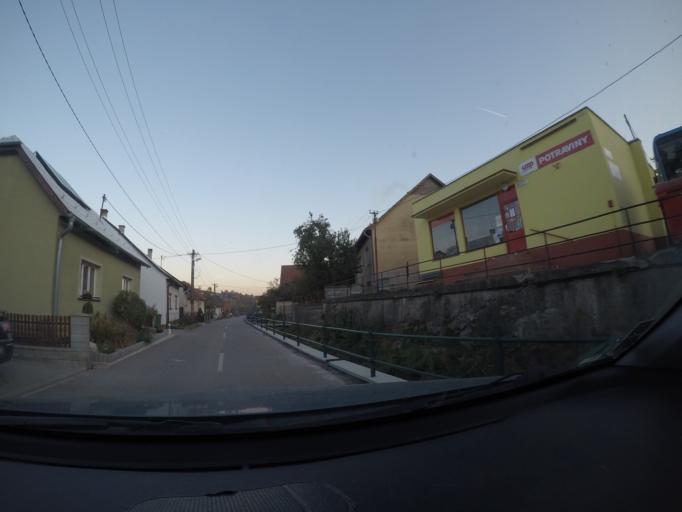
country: SK
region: Nitriansky
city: Nemsova
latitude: 48.9779
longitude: 18.0717
